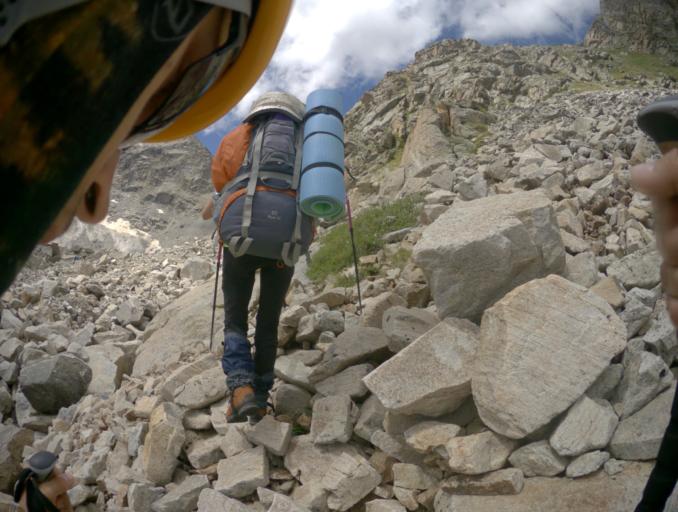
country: RU
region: Karachayevo-Cherkesiya
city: Uchkulan
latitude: 43.3240
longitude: 42.0886
